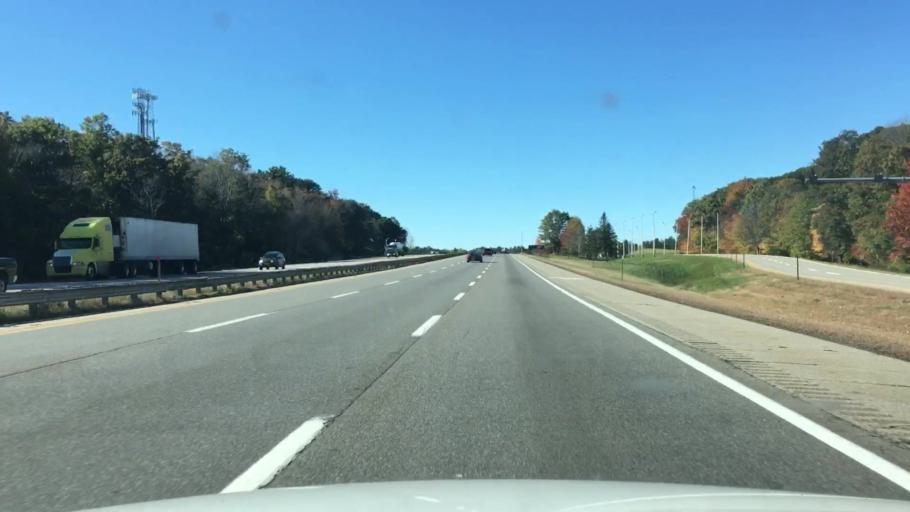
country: US
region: Maine
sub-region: York County
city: Kittery Point
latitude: 43.1378
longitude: -70.7059
